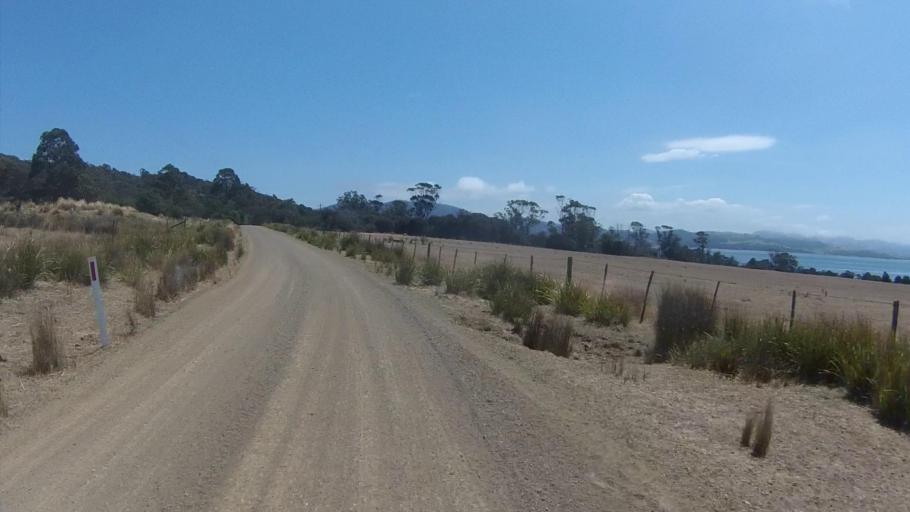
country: AU
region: Tasmania
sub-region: Sorell
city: Sorell
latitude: -42.8952
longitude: 147.8636
